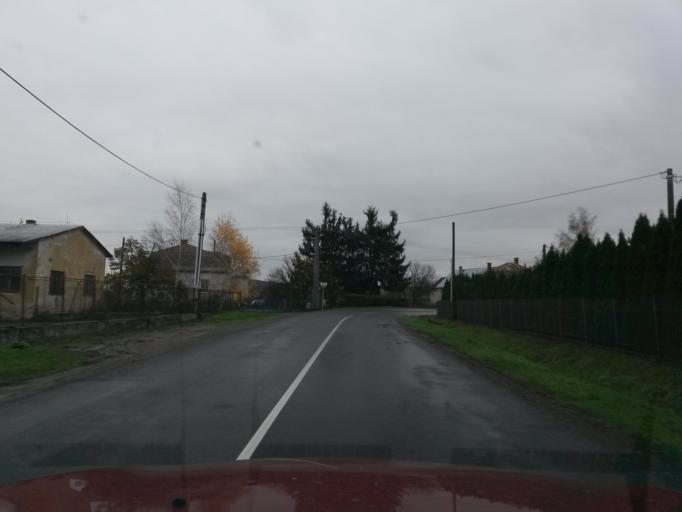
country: SK
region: Kosicky
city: Trebisov
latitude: 48.5287
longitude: 21.7395
